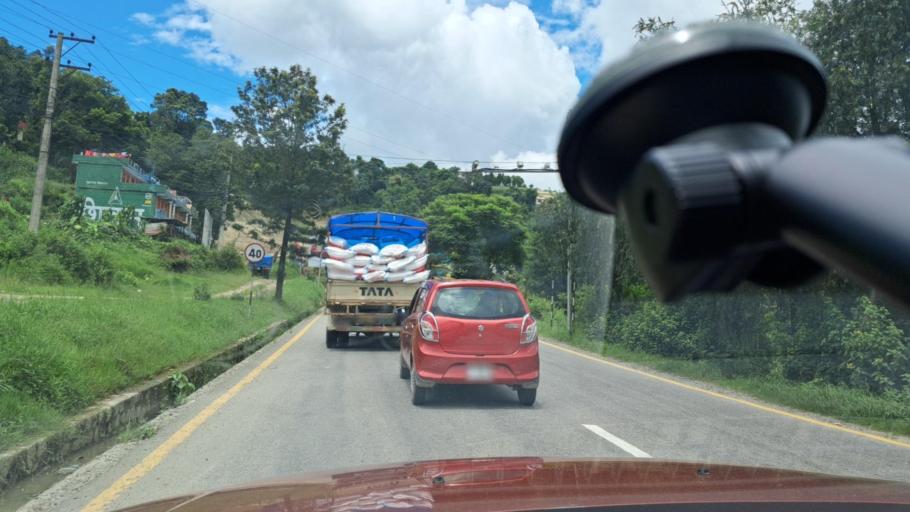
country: NP
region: Central Region
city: Banepa
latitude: 27.6256
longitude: 85.5422
